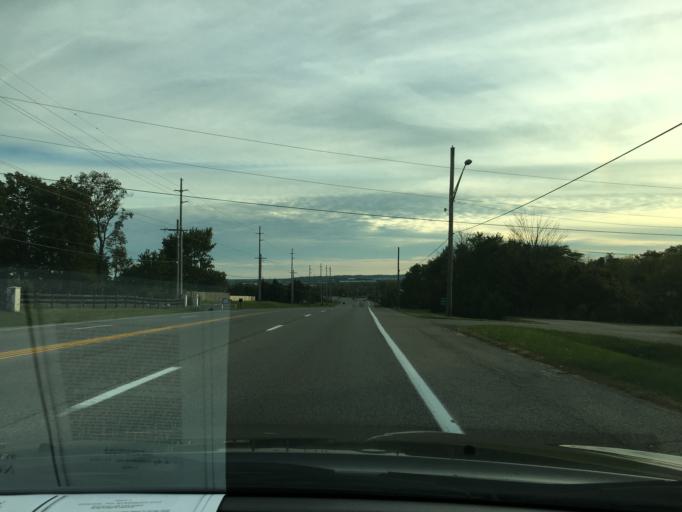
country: US
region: Ohio
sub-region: Butler County
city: Beckett Ridge
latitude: 39.3669
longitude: -84.4576
